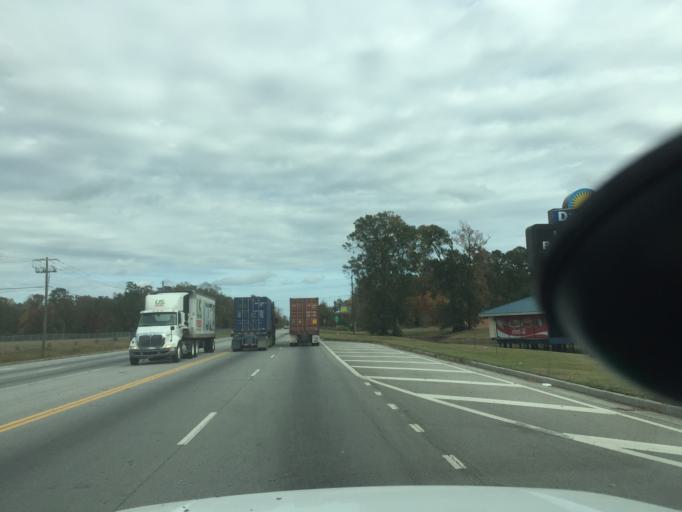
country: US
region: Georgia
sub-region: Chatham County
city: Garden City
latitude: 32.1195
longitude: -81.1891
